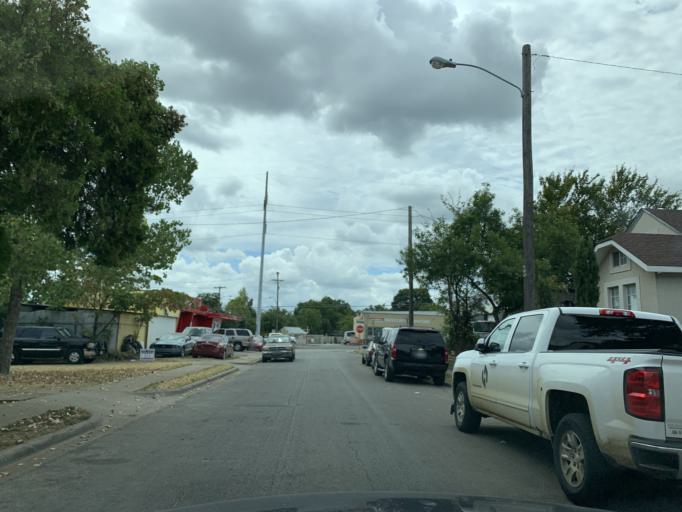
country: US
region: Texas
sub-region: Dallas County
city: Cockrell Hill
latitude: 32.7503
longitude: -96.8701
